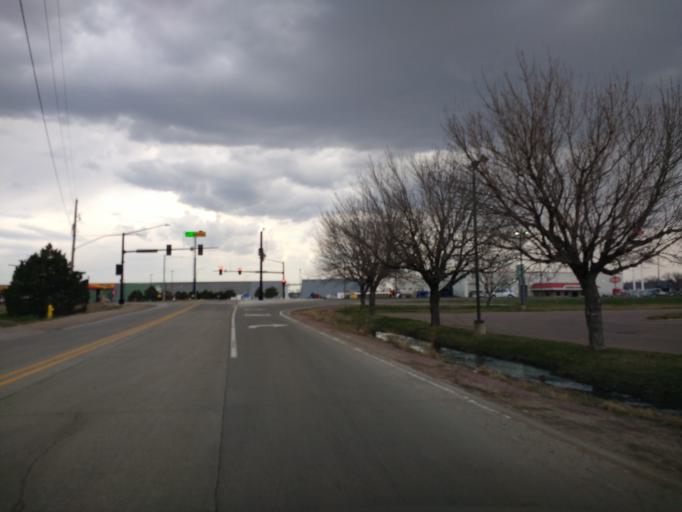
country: US
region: Iowa
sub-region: Woodbury County
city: Sergeant Bluff
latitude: 42.4332
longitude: -96.3784
